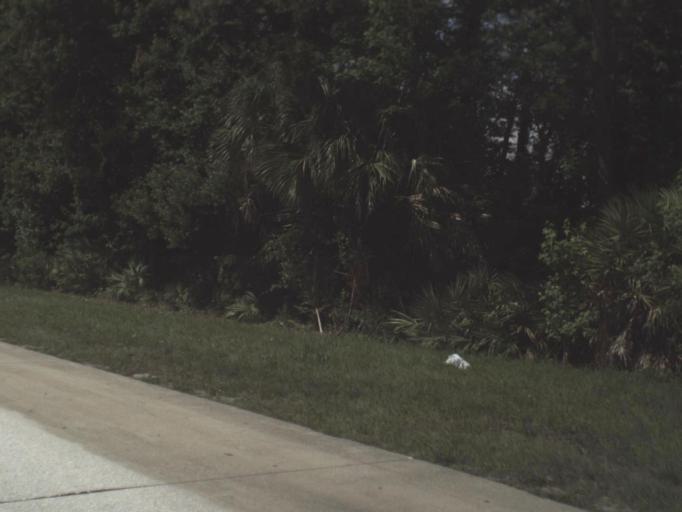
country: US
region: Florida
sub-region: Saint Johns County
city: Fruit Cove
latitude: 30.2117
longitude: -81.5651
